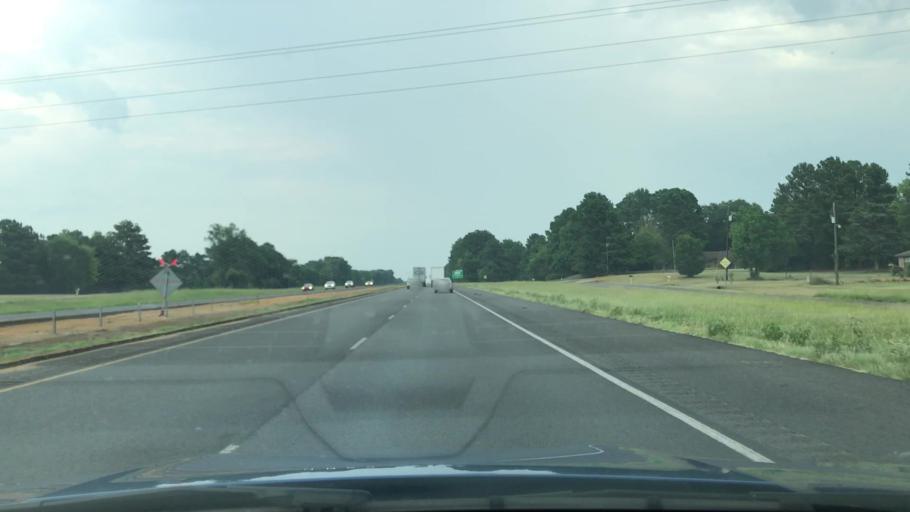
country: US
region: Texas
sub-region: Harrison County
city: Marshall
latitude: 32.4947
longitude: -94.2675
